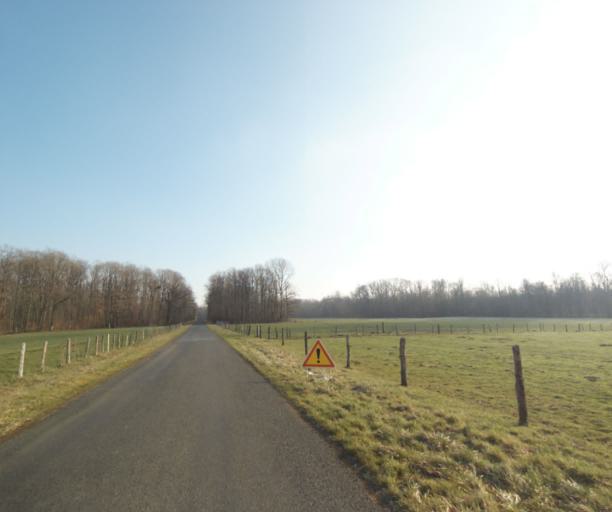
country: FR
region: Champagne-Ardenne
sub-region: Departement de la Haute-Marne
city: Laneuville-a-Remy
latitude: 48.4585
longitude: 4.9259
